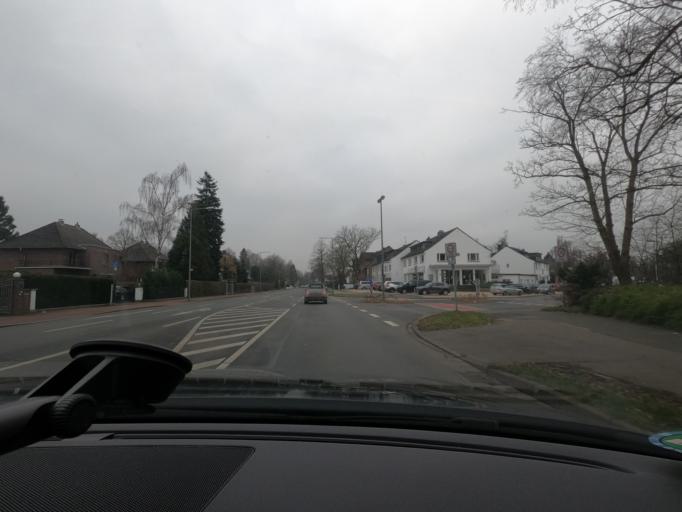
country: DE
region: North Rhine-Westphalia
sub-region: Regierungsbezirk Dusseldorf
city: Krefeld
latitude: 51.3557
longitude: 6.5735
